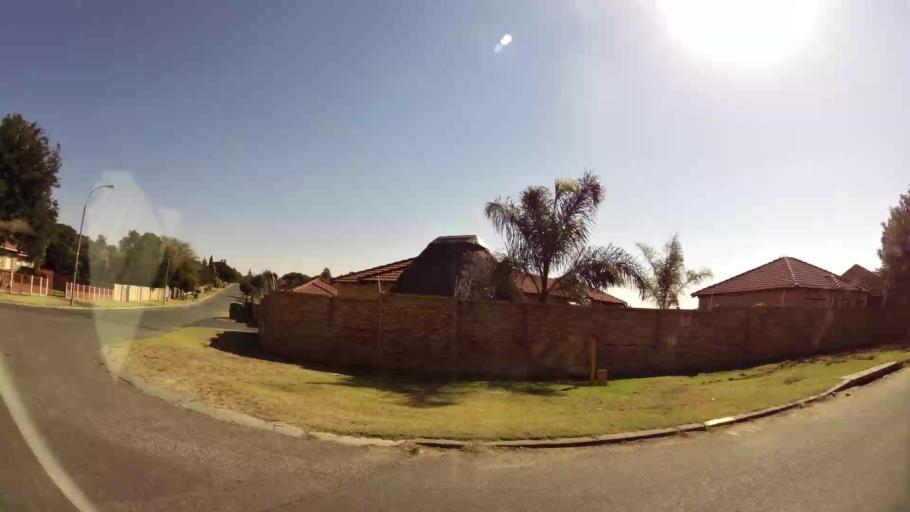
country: ZA
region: Gauteng
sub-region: Ekurhuleni Metropolitan Municipality
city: Tembisa
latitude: -26.0528
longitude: 28.2223
